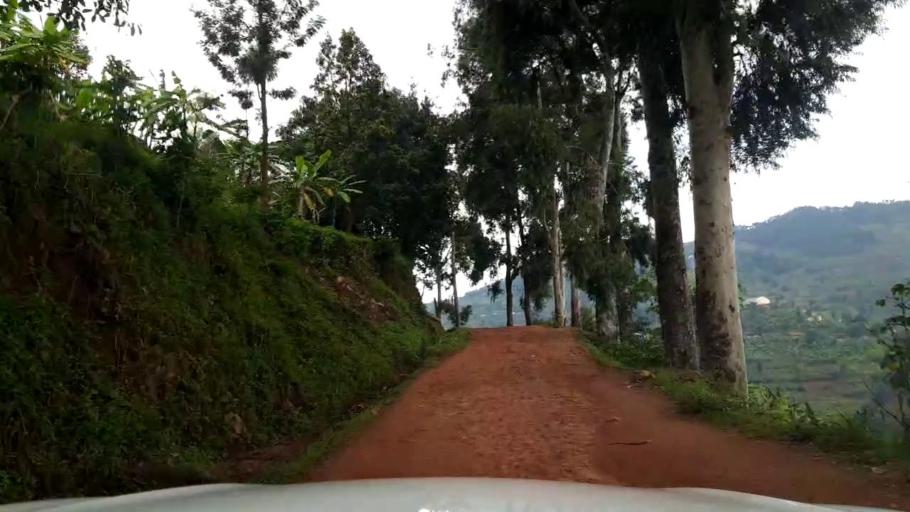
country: UG
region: Western Region
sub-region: Kisoro District
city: Kisoro
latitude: -1.3937
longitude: 29.7994
